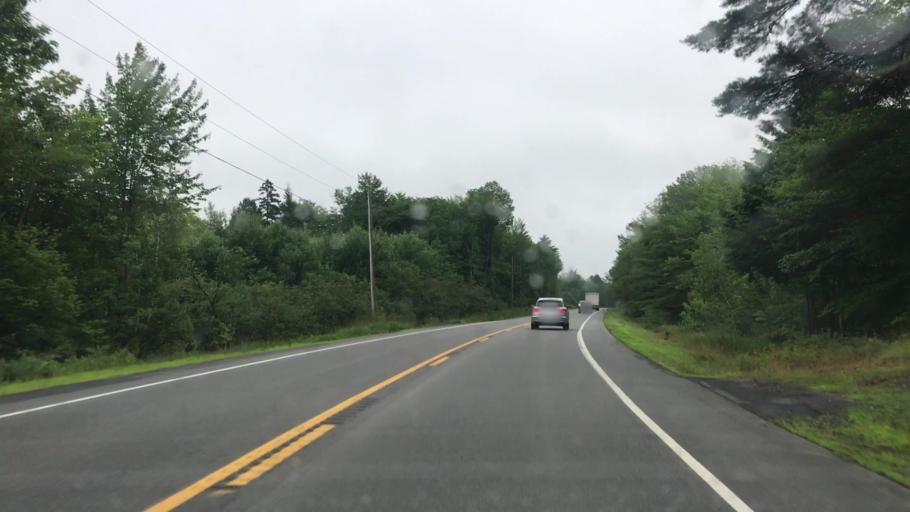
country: US
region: Maine
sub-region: Knox County
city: Washington
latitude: 44.2466
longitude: -69.3927
